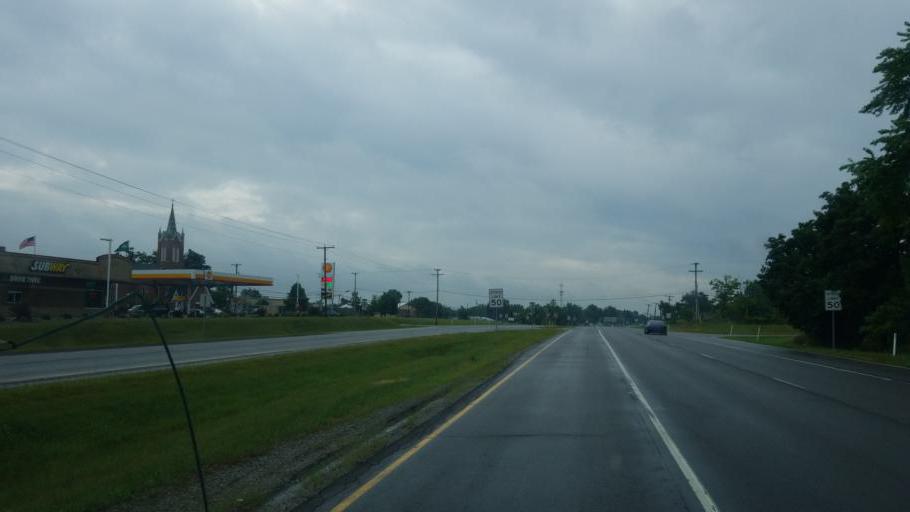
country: US
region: Indiana
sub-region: Allen County
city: New Haven
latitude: 40.9802
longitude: -85.0847
